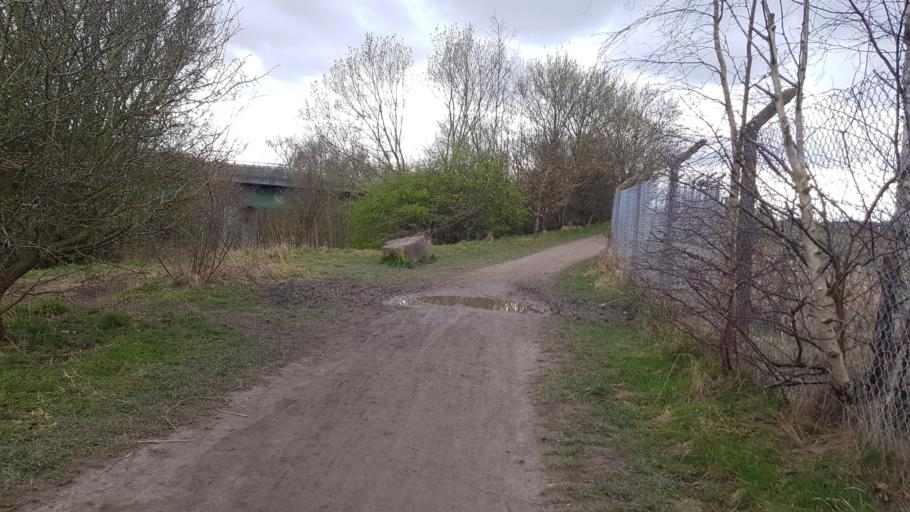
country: GB
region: England
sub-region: City and Borough of Leeds
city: Swillington
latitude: 53.7450
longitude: -1.3990
